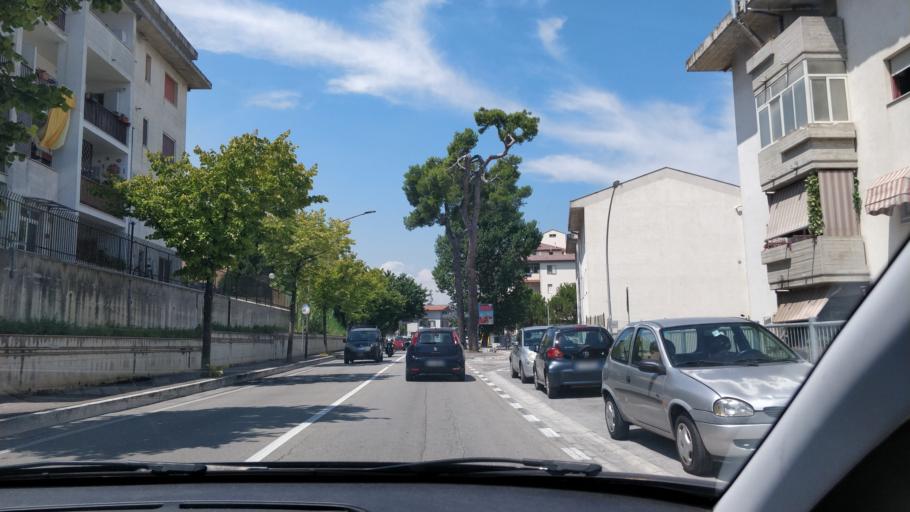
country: IT
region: Abruzzo
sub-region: Provincia di Chieti
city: Francavilla al Mare
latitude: 42.4077
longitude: 14.3088
